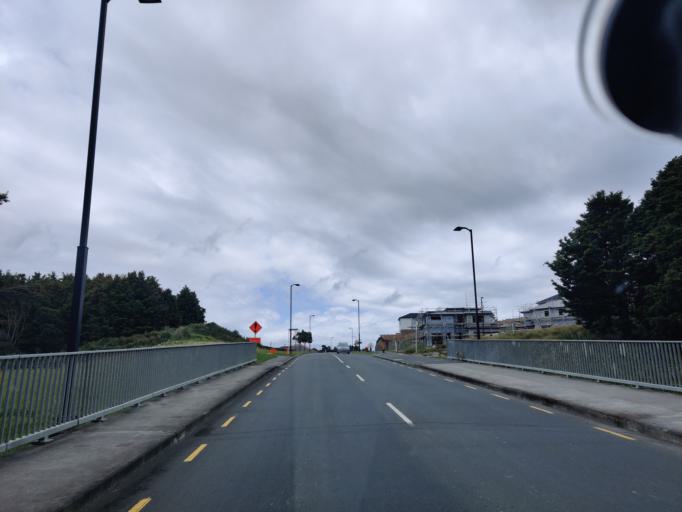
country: NZ
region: Auckland
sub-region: Auckland
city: Rothesay Bay
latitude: -36.5957
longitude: 174.6712
